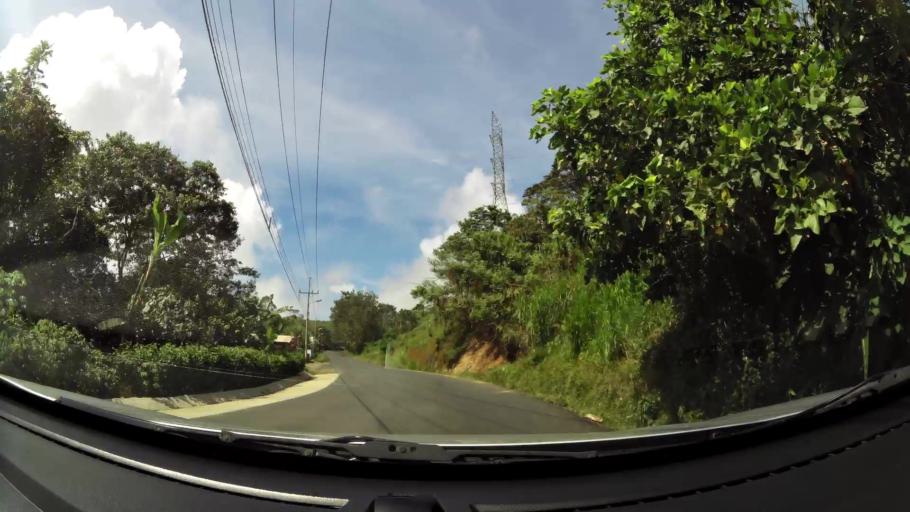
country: CR
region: San Jose
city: San Isidro
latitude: 9.3279
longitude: -83.7480
